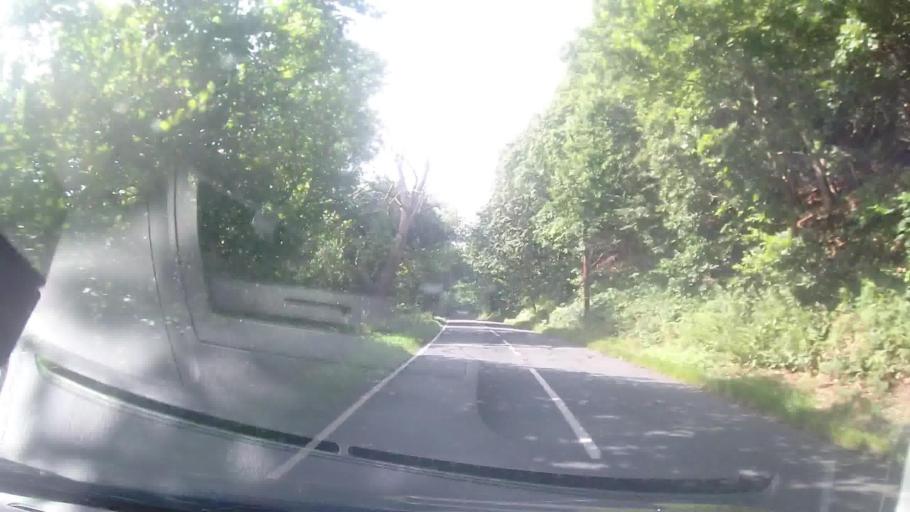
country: GB
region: Wales
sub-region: Sir Powys
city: Knighton
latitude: 52.3560
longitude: -3.0386
